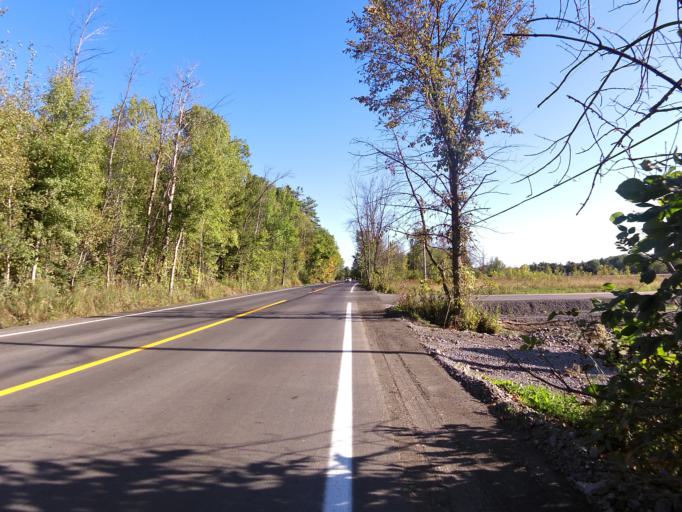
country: CA
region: Quebec
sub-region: Outaouais
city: Wakefield
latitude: 45.4934
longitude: -75.8932
